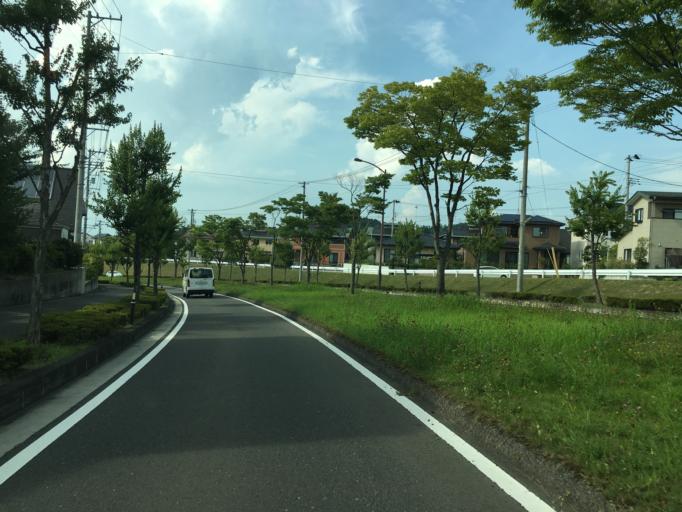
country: JP
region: Fukushima
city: Koriyama
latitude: 37.3872
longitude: 140.4355
